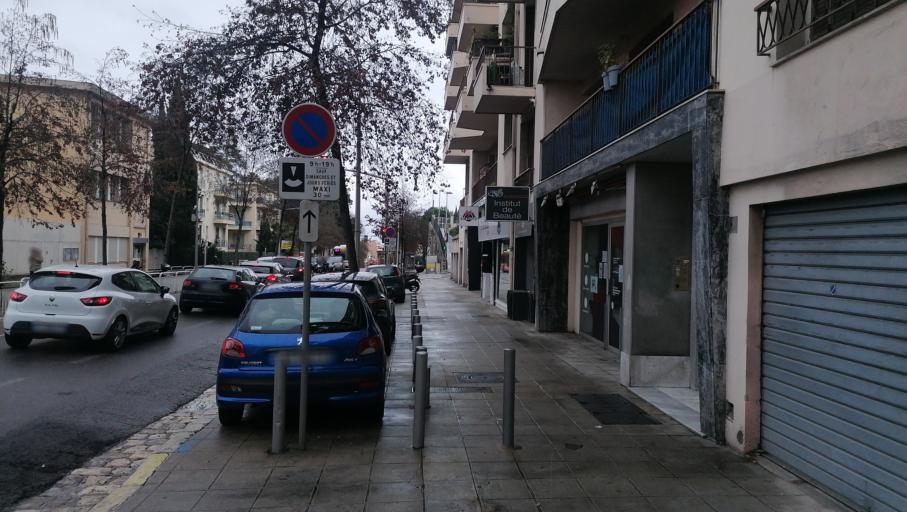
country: FR
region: Provence-Alpes-Cote d'Azur
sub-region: Departement des Alpes-Maritimes
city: Nice
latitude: 43.7159
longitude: 7.2537
